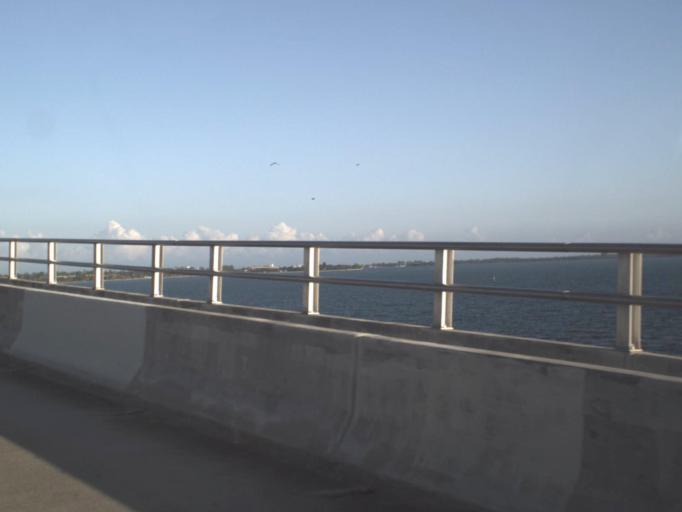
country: US
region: Florida
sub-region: Miami-Dade County
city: Miami
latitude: 25.7463
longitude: -80.1882
